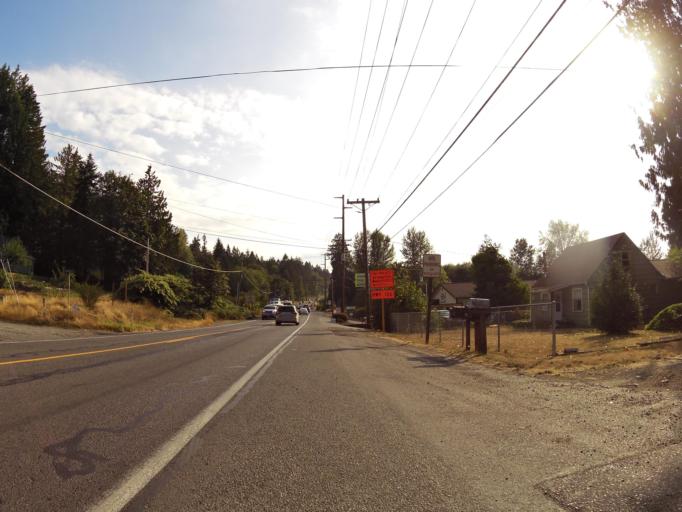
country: US
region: Washington
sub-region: Mason County
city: Belfair
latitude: 47.4352
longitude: -122.8391
